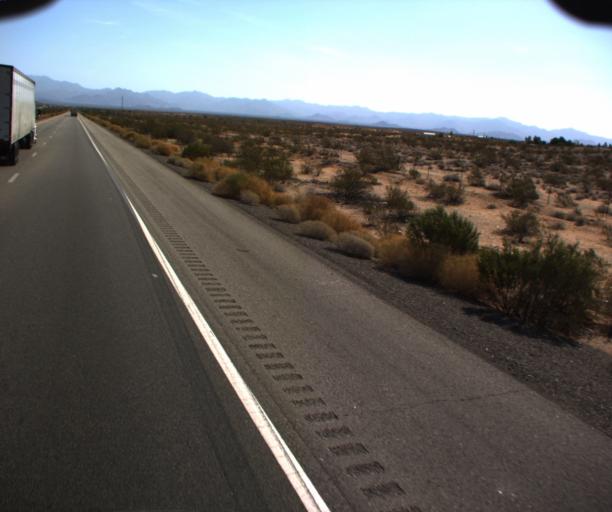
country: US
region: Arizona
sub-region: Mohave County
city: Desert Hills
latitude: 34.7562
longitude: -114.2141
